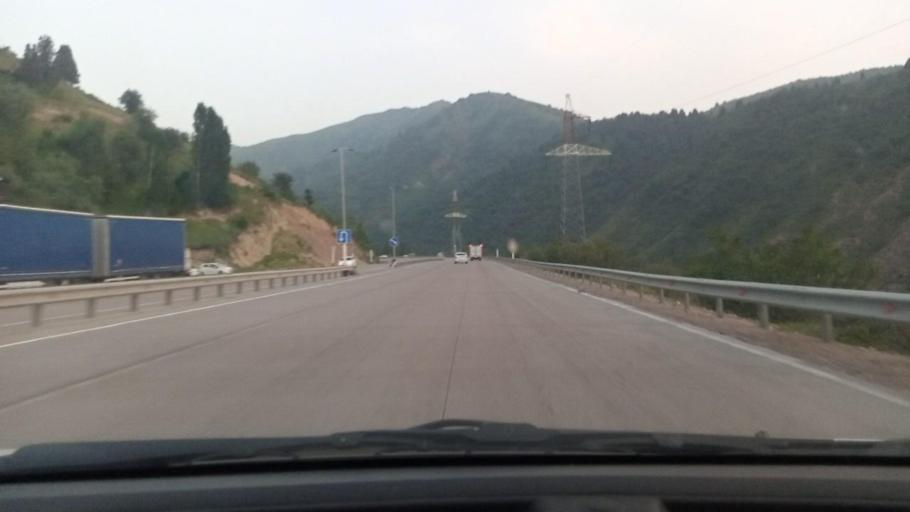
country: UZ
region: Toshkent
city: Angren
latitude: 41.1485
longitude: 70.4462
